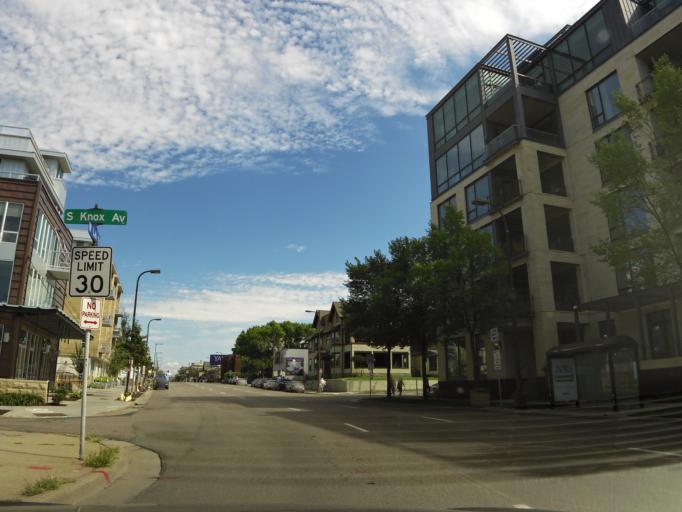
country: US
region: Minnesota
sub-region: Hennepin County
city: Saint Louis Park
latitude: 44.9485
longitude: -93.3052
